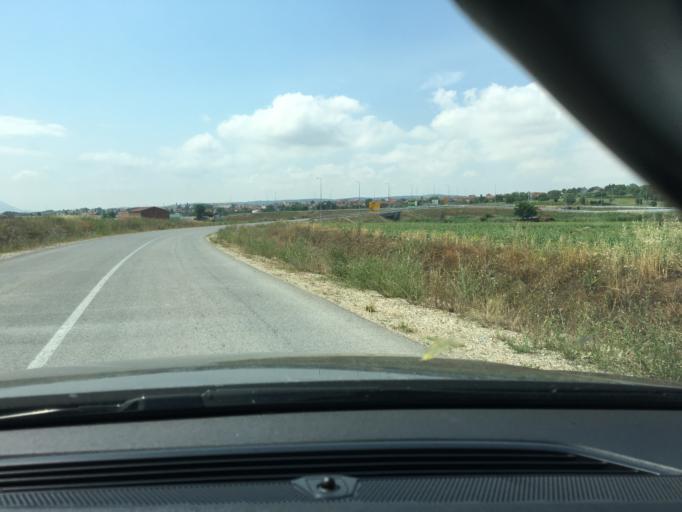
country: MK
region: Sveti Nikole
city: Sveti Nikole
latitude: 41.8807
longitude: 21.9395
